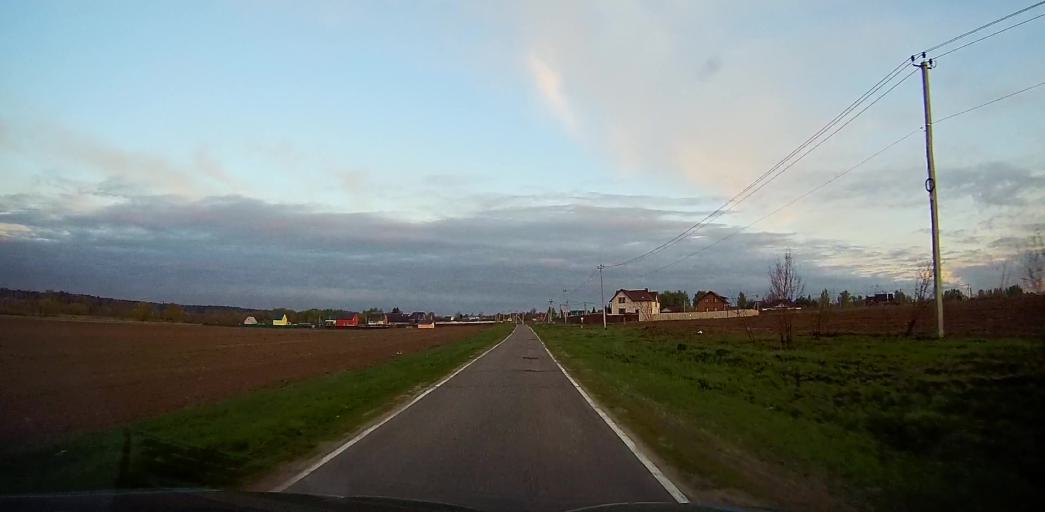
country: RU
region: Moskovskaya
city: Peski
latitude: 55.2162
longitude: 38.7387
